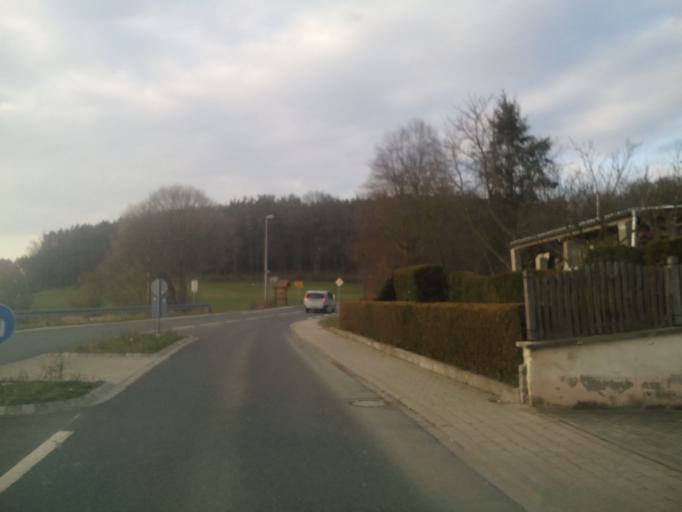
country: DE
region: Bavaria
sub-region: Regierungsbezirk Mittelfranken
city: Hochstadt an der Aisch
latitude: 49.7178
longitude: 10.8172
